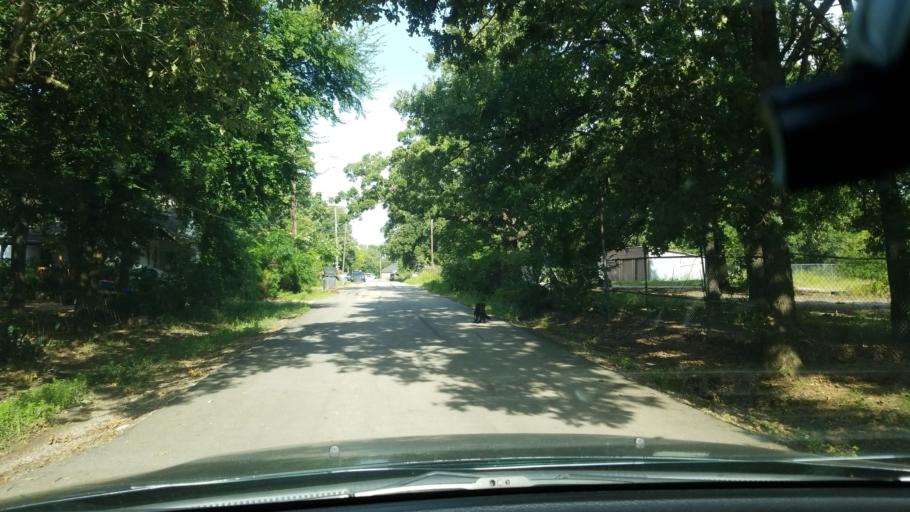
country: US
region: Texas
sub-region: Dallas County
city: Balch Springs
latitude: 32.7143
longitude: -96.6288
